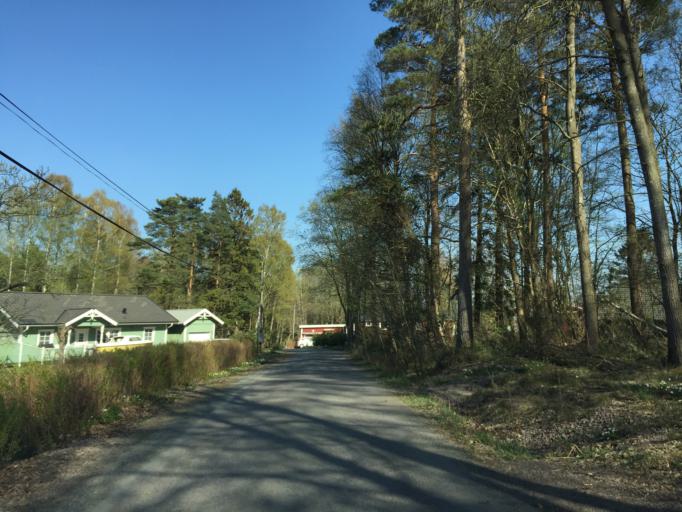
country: SE
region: Vaestra Goetaland
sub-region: Ale Kommun
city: Surte
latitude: 57.8160
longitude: 11.9863
